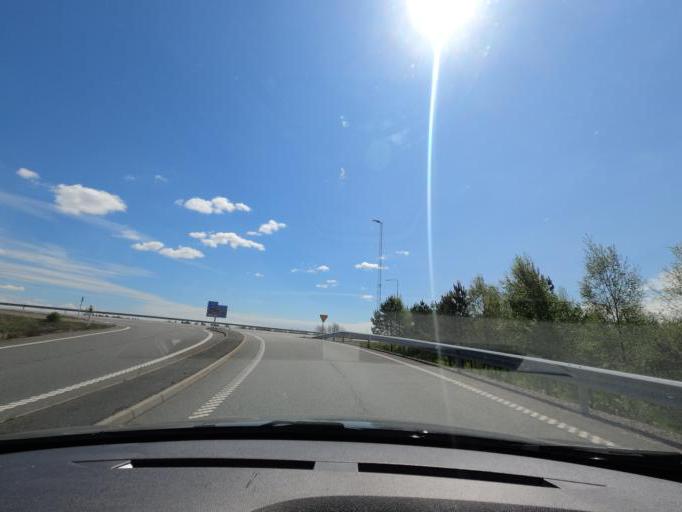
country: SE
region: Joenkoeping
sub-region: Varnamo Kommun
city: Bredaryd
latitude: 57.1804
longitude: 13.7468
